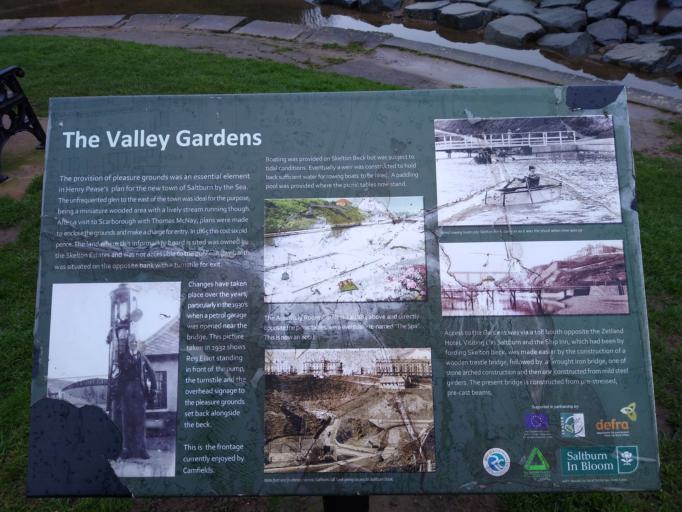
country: GB
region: England
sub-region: Redcar and Cleveland
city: Saltburn-by-the-Sea
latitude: 54.5843
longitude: -0.9682
